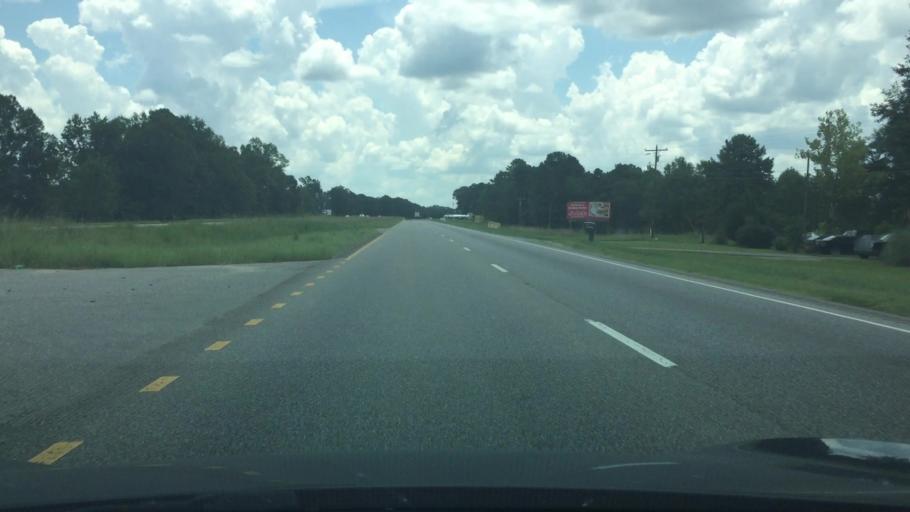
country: US
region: Alabama
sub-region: Montgomery County
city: Taylor
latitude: 32.0491
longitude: -86.0412
